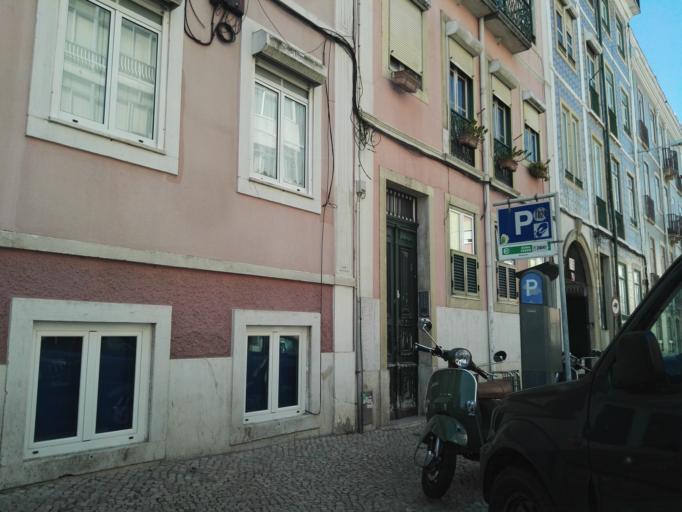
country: PT
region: Lisbon
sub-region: Lisbon
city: Lisbon
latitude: 38.7165
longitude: -9.1644
